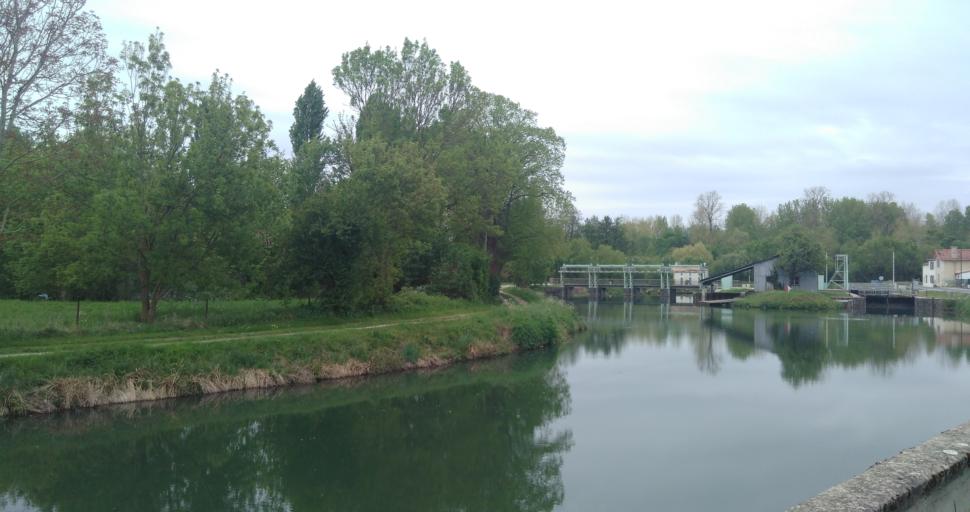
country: FR
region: Poitou-Charentes
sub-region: Departement des Deux-Sevres
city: Coulon
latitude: 46.3125
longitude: -0.6154
